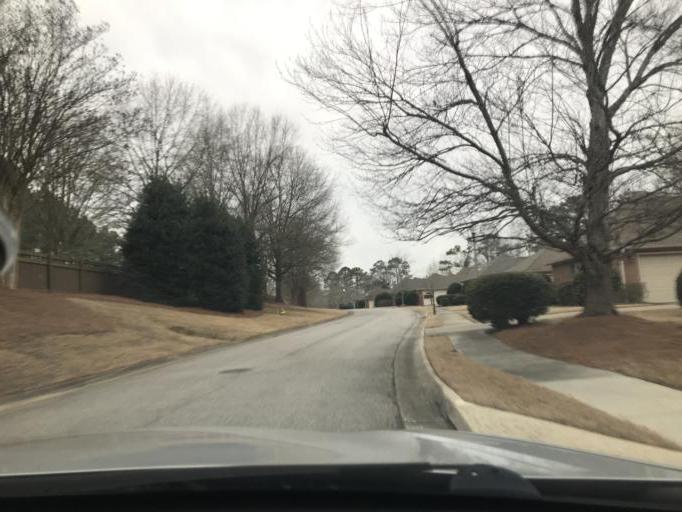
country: US
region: Alabama
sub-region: Jefferson County
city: Cahaba Heights
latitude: 33.4758
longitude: -86.6908
